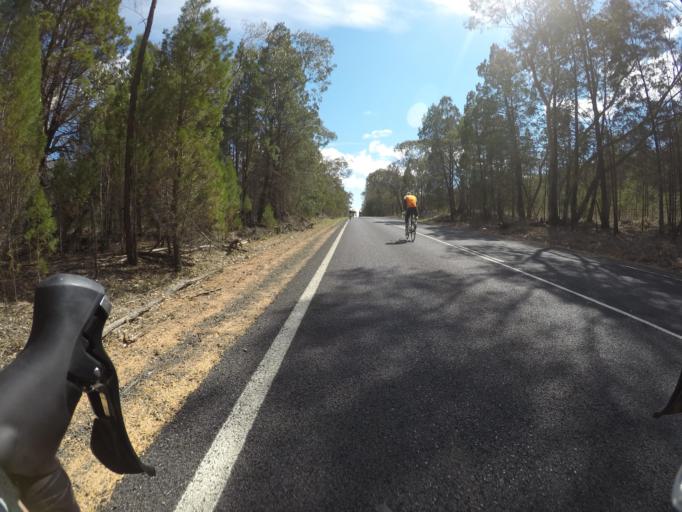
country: AU
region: New South Wales
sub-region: Parkes
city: Peak Hill
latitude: -32.6813
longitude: 148.5577
